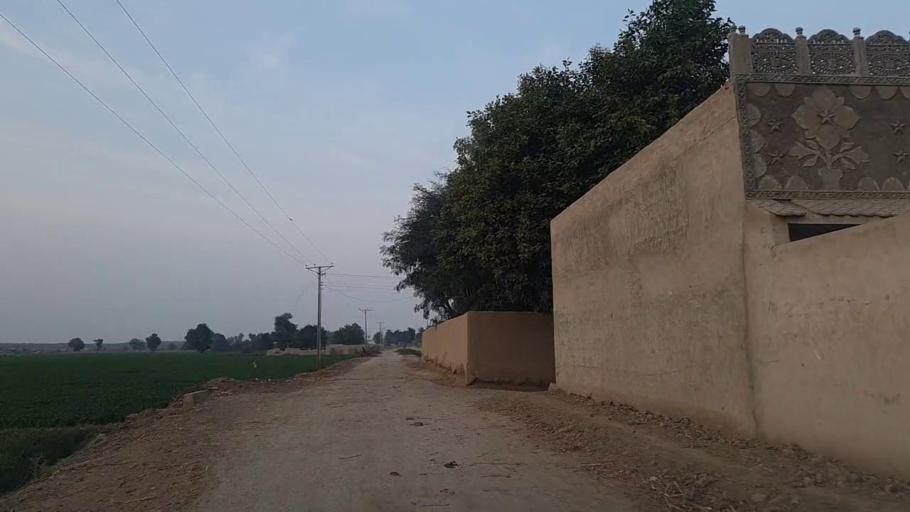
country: PK
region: Sindh
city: Jam Sahib
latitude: 26.4724
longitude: 68.5481
